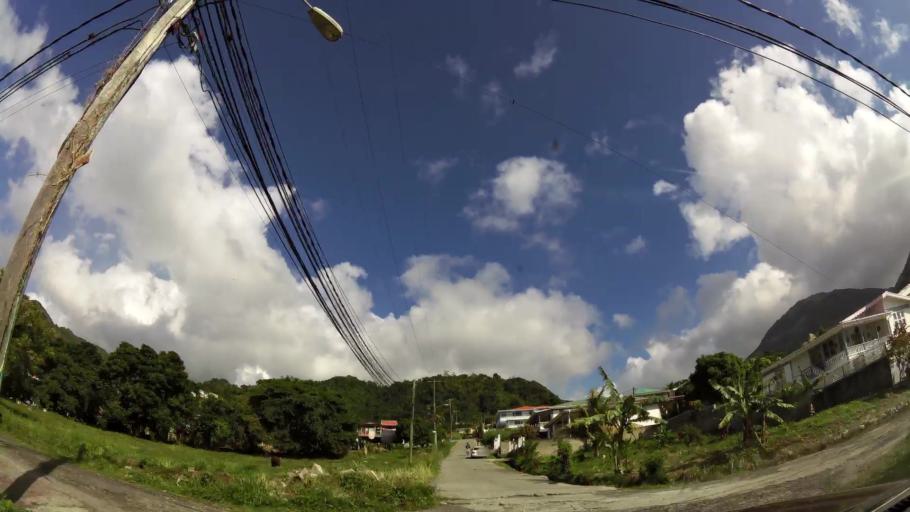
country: DM
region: Saint Luke
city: Pointe Michel
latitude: 15.2811
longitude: -61.3731
